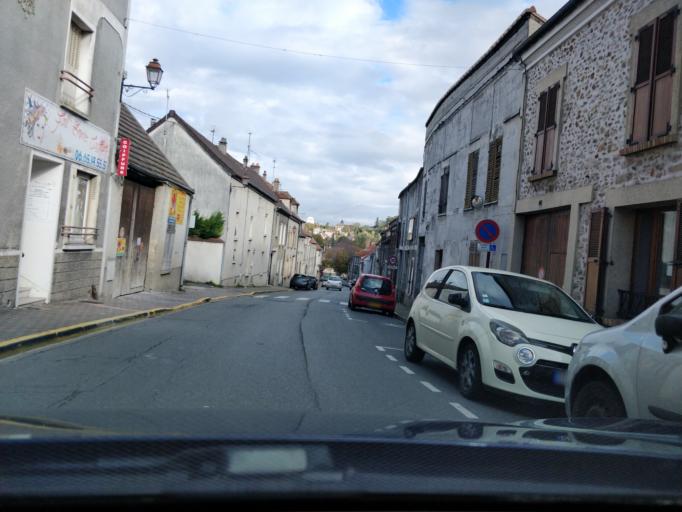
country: FR
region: Ile-de-France
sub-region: Departement de l'Essonne
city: Linas
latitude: 48.6291
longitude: 2.2639
